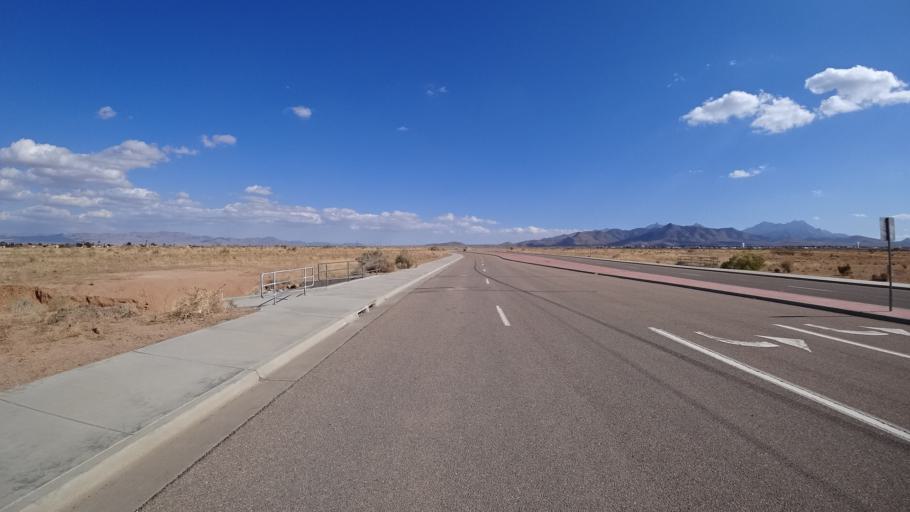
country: US
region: Arizona
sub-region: Mohave County
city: New Kingman-Butler
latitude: 35.2181
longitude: -113.9831
